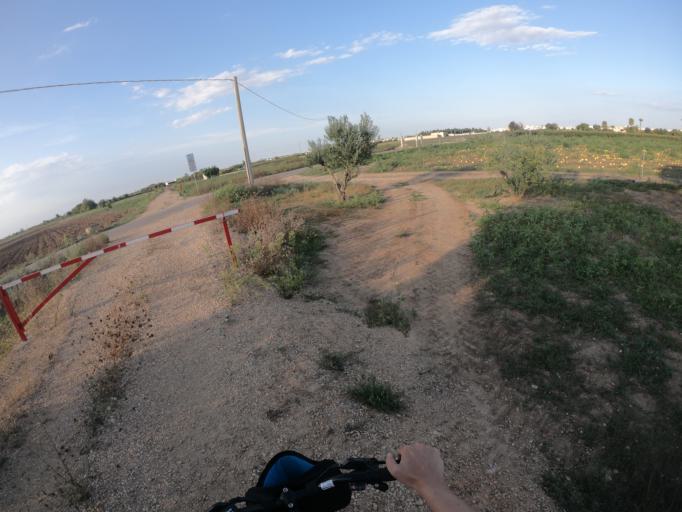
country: IT
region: Apulia
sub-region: Provincia di Lecce
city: Nardo
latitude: 40.1751
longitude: 18.0127
